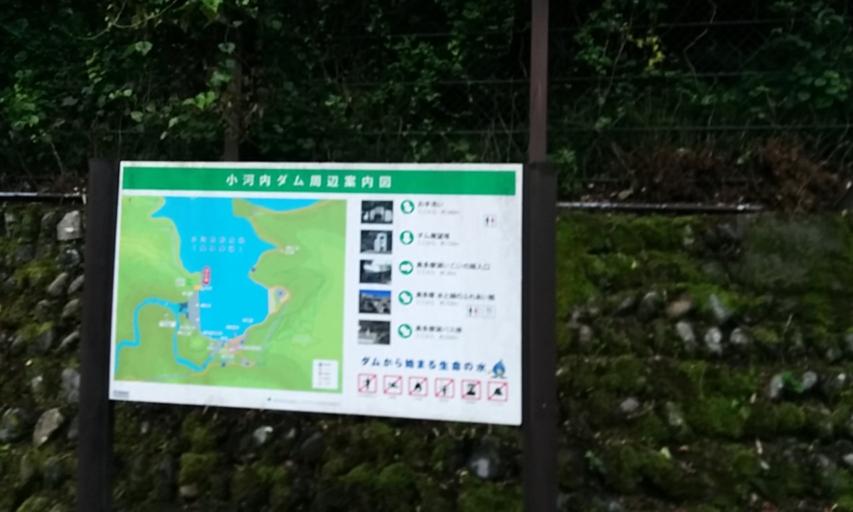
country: JP
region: Tokyo
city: Itsukaichi
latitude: 35.7880
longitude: 139.0505
